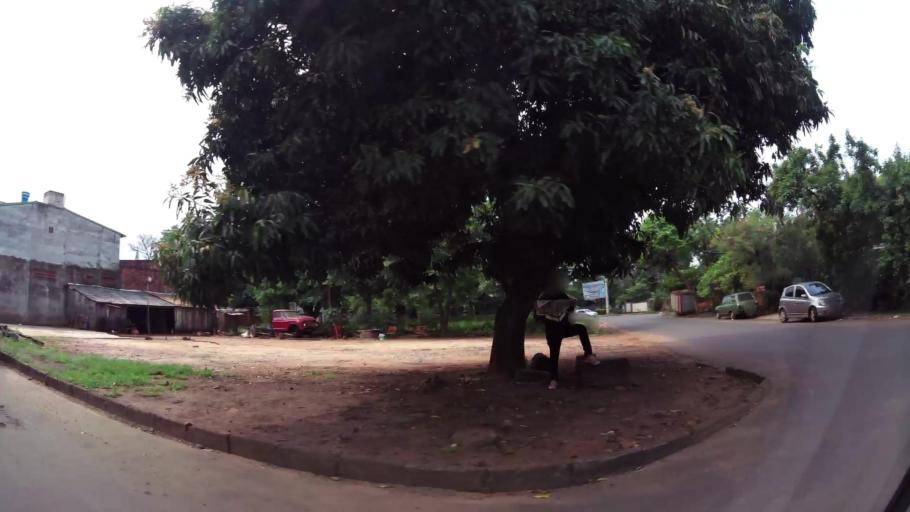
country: PY
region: Alto Parana
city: Presidente Franco
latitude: -25.5305
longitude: -54.6122
